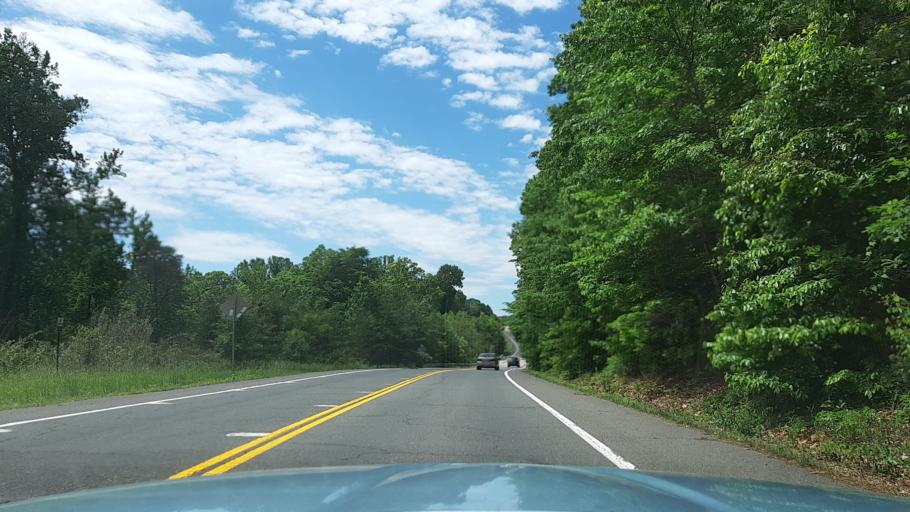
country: US
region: Virginia
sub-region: Fairfax County
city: Burke
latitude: 38.7490
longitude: -77.2811
